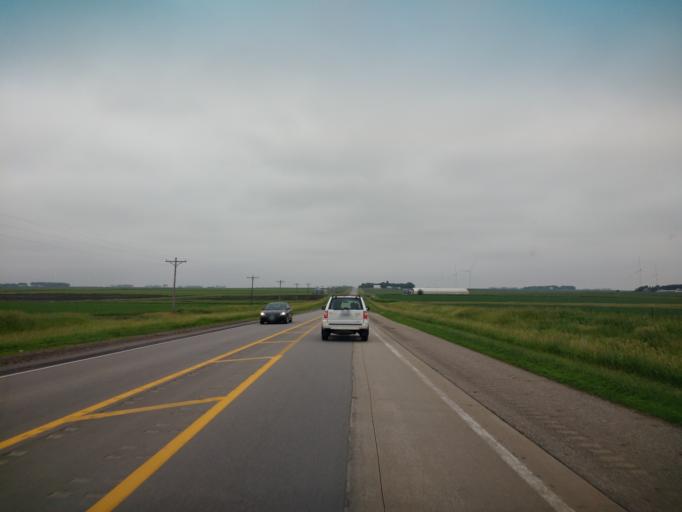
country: US
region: Iowa
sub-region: O'Brien County
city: Hartley
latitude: 43.1850
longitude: -95.5086
